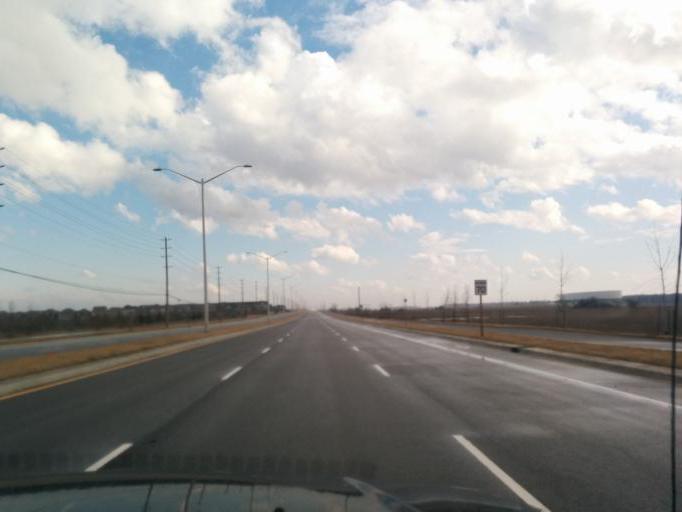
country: CA
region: Ontario
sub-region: Halton
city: Milton
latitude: 43.4844
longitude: -79.8818
